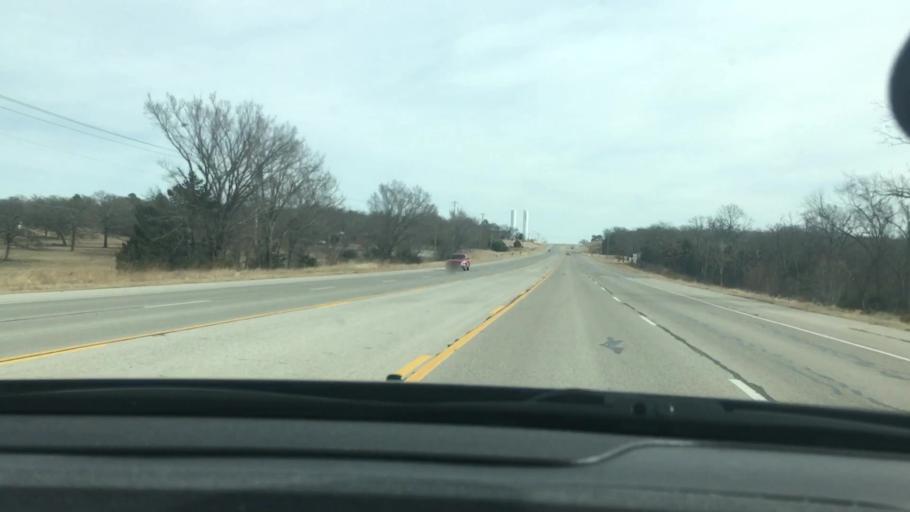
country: US
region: Oklahoma
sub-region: Carter County
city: Dickson
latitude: 34.1871
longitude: -97.0097
